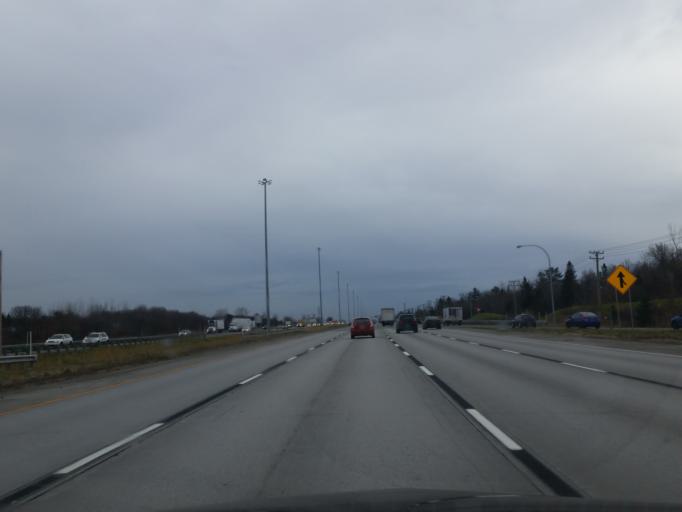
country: CA
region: Quebec
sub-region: Laurentides
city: Blainville
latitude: 45.6543
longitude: -73.8800
